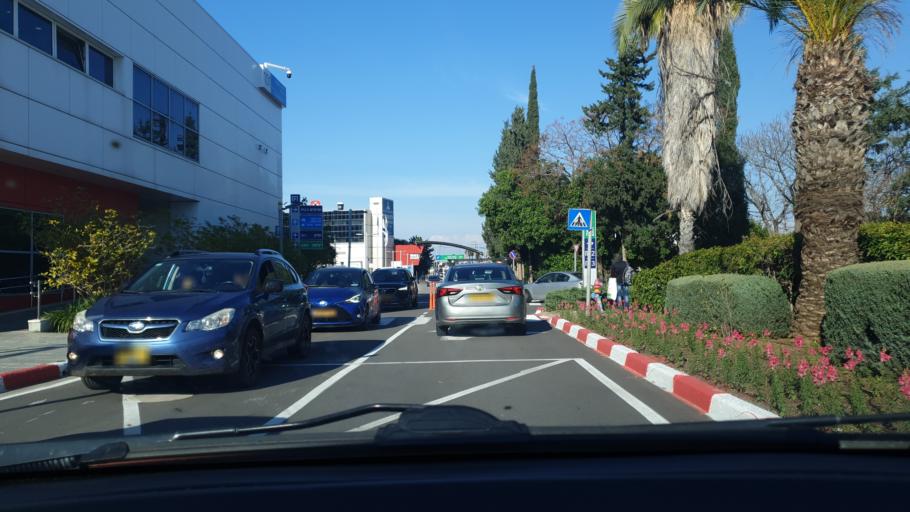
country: IL
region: Central District
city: Kefar Habad
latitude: 31.9667
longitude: 34.8419
